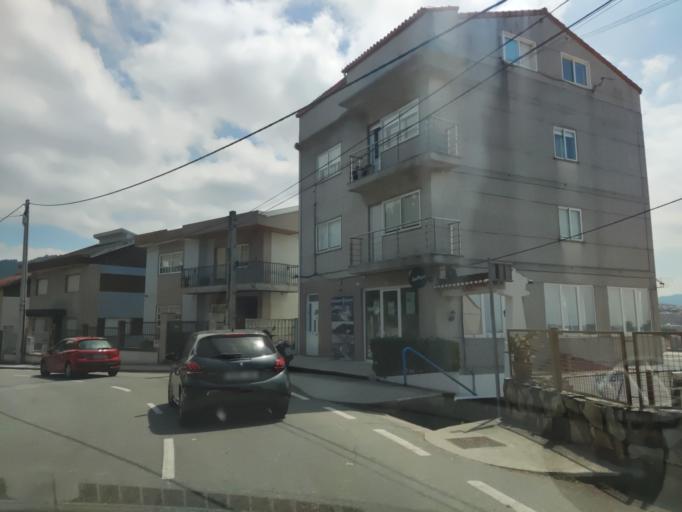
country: ES
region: Galicia
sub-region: Provincia de Pontevedra
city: Vigo
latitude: 42.2540
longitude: -8.7027
